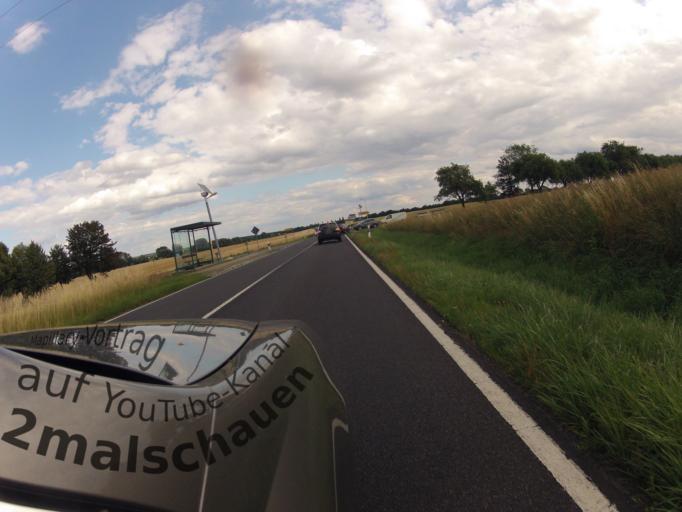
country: DE
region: Mecklenburg-Vorpommern
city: Seebad Bansin
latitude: 53.8951
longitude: 14.0681
